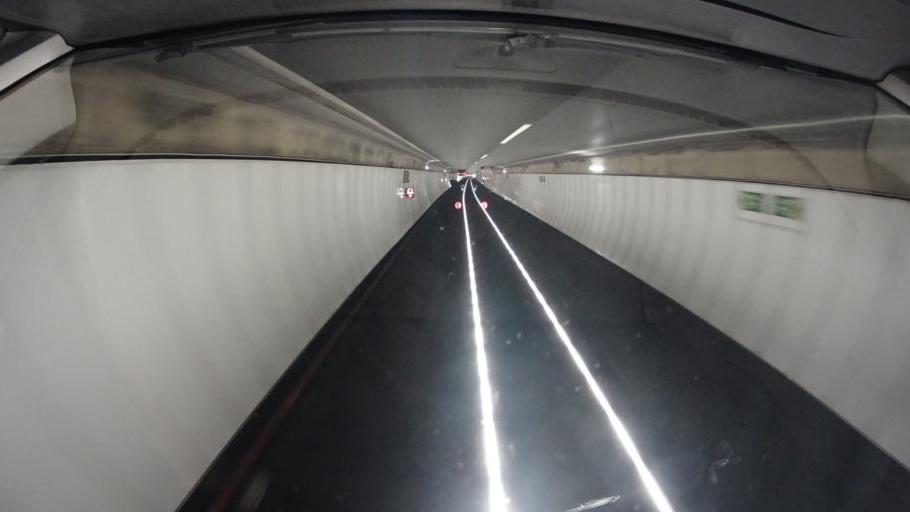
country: ES
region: Basque Country
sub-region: Bizkaia
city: Basauri
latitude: 43.2327
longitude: -2.9006
